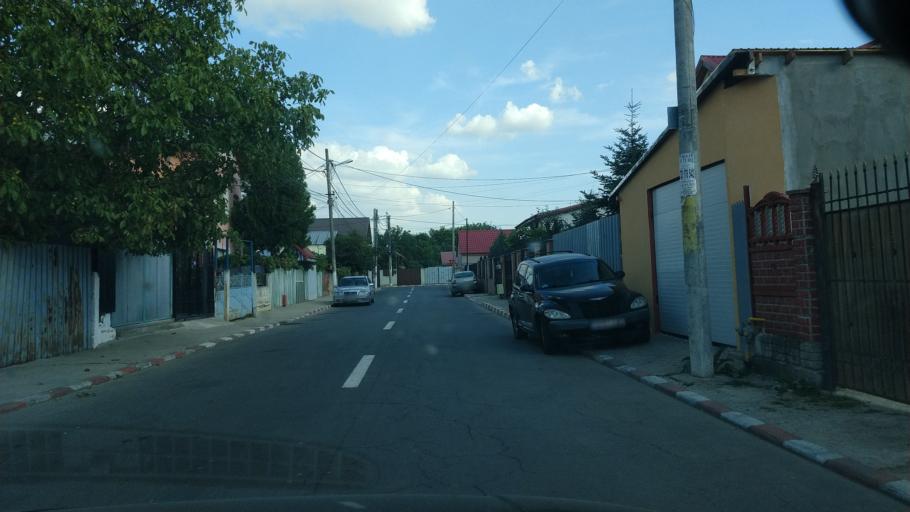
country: RO
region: Ilfov
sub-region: Voluntari City
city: Voluntari
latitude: 44.4923
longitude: 26.1641
